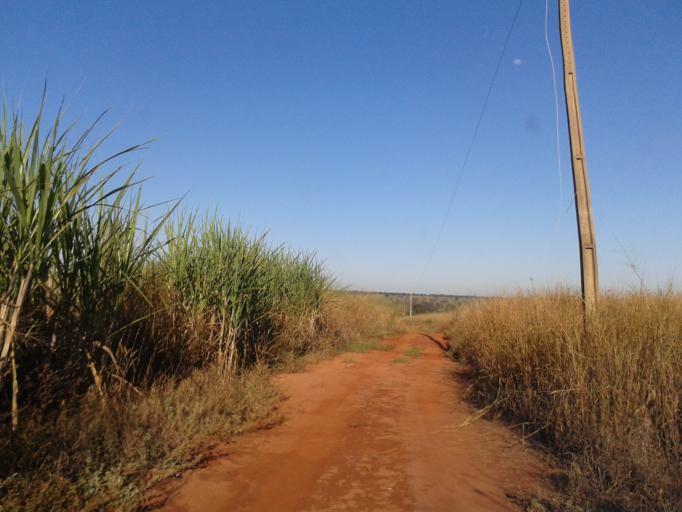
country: BR
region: Minas Gerais
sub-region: Santa Vitoria
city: Santa Vitoria
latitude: -19.0215
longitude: -50.3626
